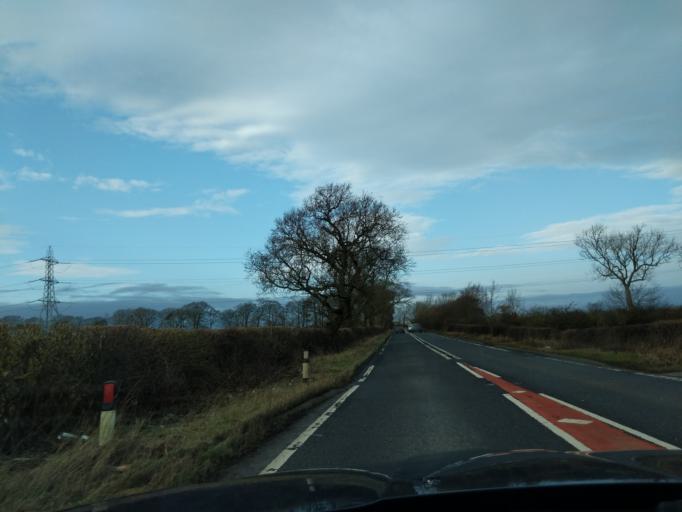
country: GB
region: England
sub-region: Northumberland
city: Darras Hall
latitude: 55.0575
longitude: -1.7677
